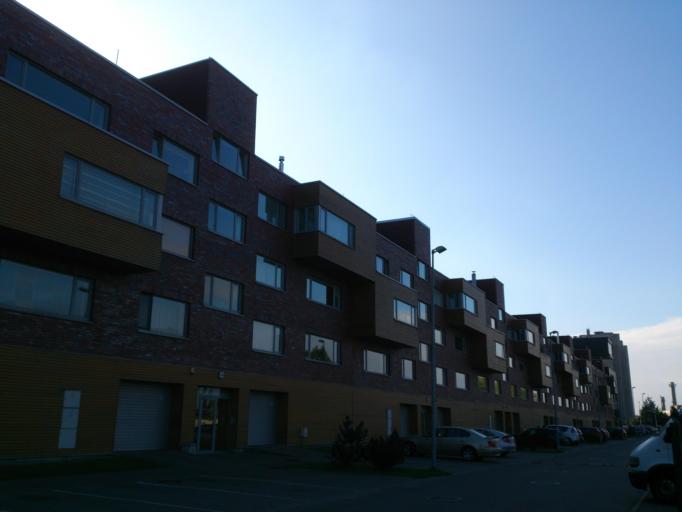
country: LT
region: Kauno apskritis
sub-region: Kaunas
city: Aleksotas
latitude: 54.8749
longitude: 23.9095
